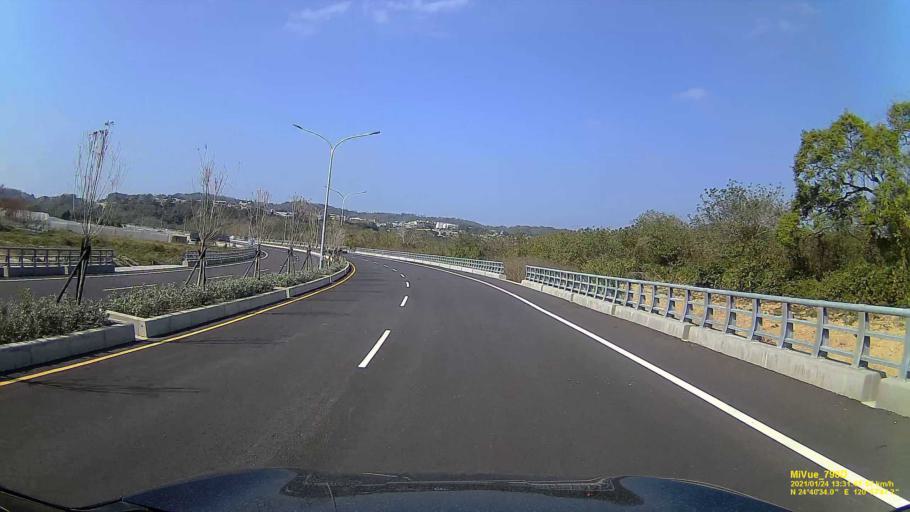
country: TW
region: Taiwan
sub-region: Hsinchu
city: Hsinchu
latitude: 24.6764
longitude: 120.9630
